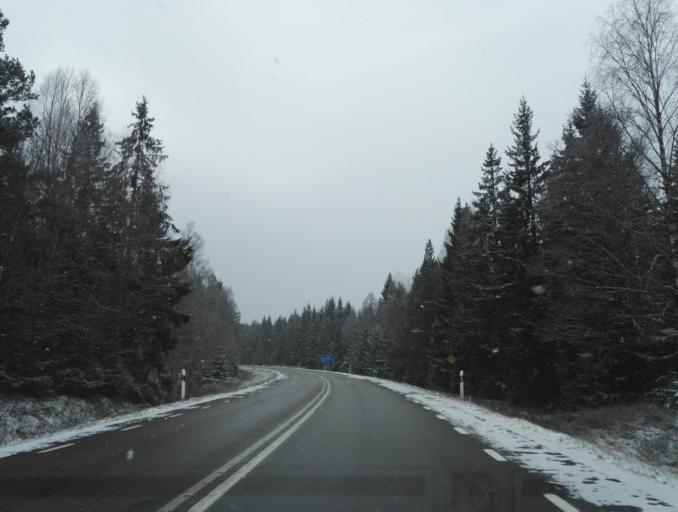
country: SE
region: Kronoberg
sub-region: Uppvidinge Kommun
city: Lenhovda
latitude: 56.9205
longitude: 15.3645
